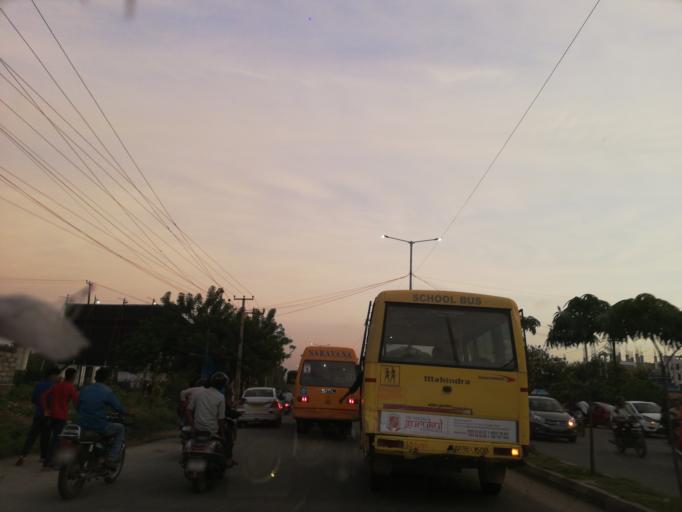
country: IN
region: Telangana
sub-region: Rangareddi
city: Kukatpalli
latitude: 17.5037
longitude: 78.3620
